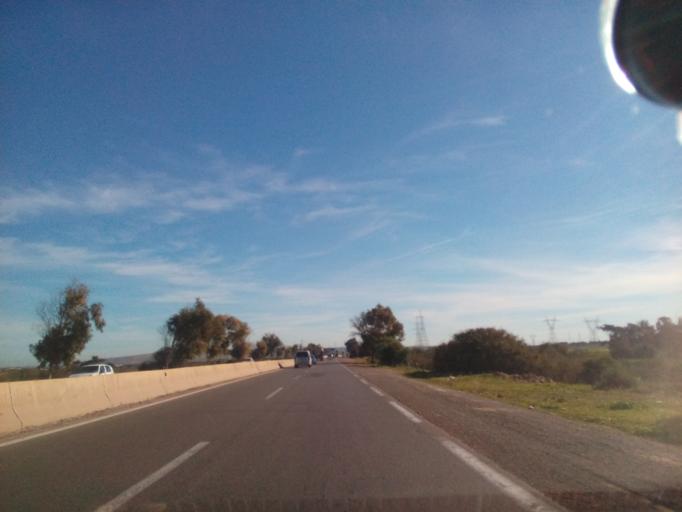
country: DZ
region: Oran
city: Ain el Bya
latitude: 35.7834
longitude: -0.1420
